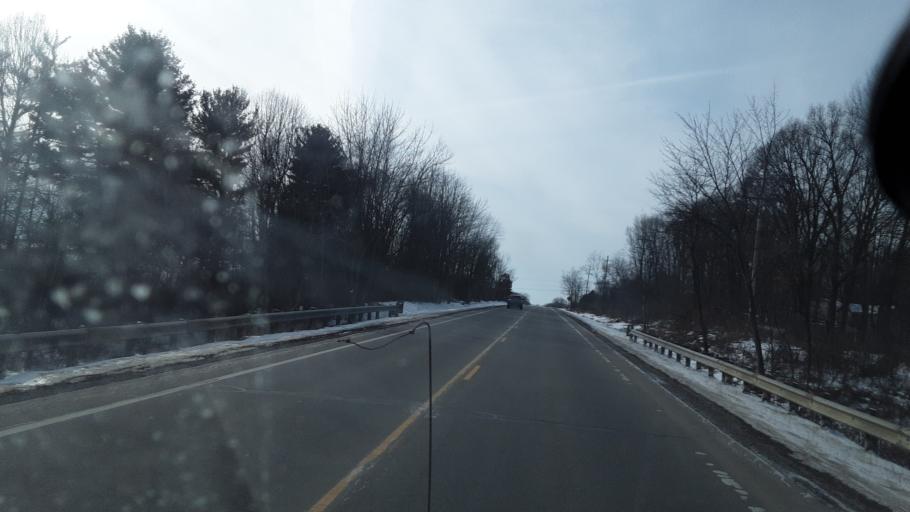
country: US
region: Ohio
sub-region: Summit County
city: Mogadore
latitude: 41.0301
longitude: -81.4022
